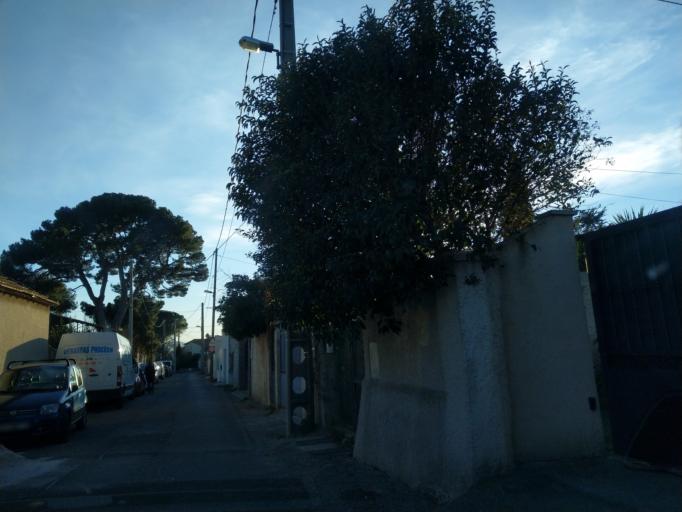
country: FR
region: Provence-Alpes-Cote d'Azur
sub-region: Departement des Bouches-du-Rhone
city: Plan-de-Cuques
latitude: 43.3574
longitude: 5.4625
